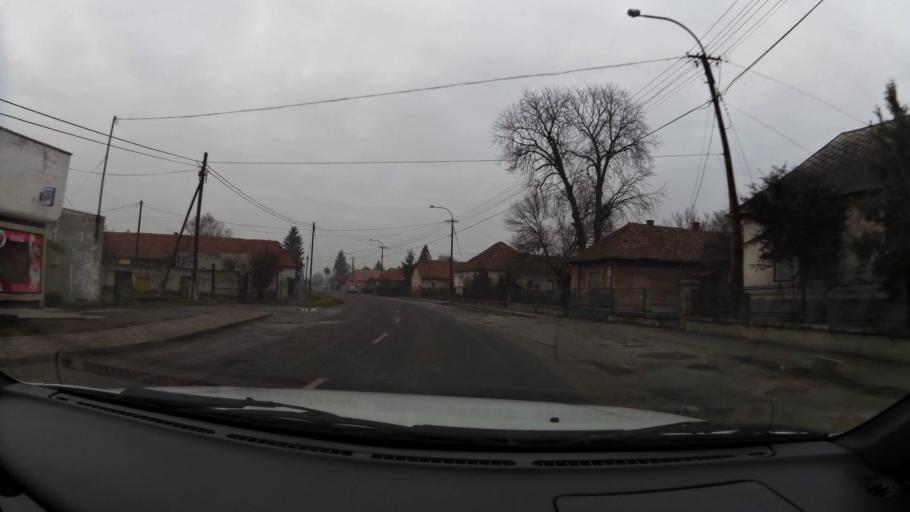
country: HU
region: Borsod-Abauj-Zemplen
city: Izsofalva
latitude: 48.3071
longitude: 20.6543
